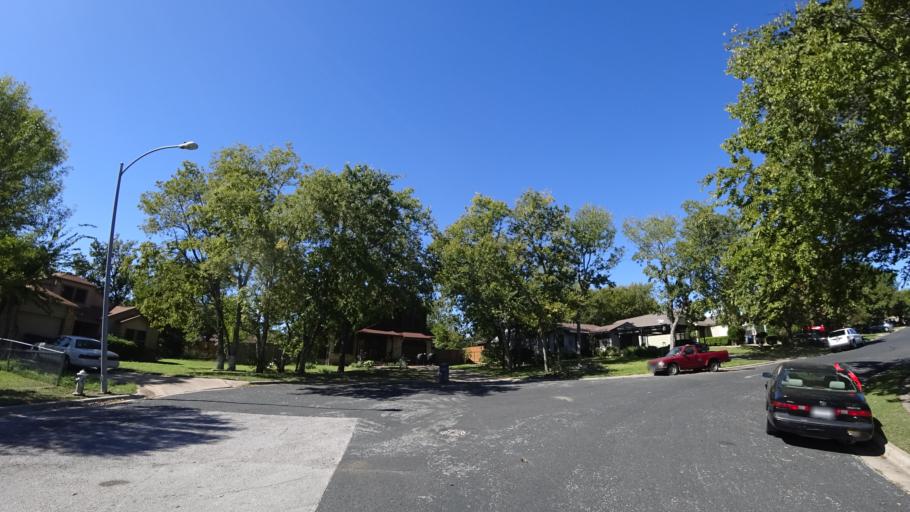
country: US
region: Texas
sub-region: Travis County
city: Hornsby Bend
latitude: 30.2993
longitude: -97.6424
